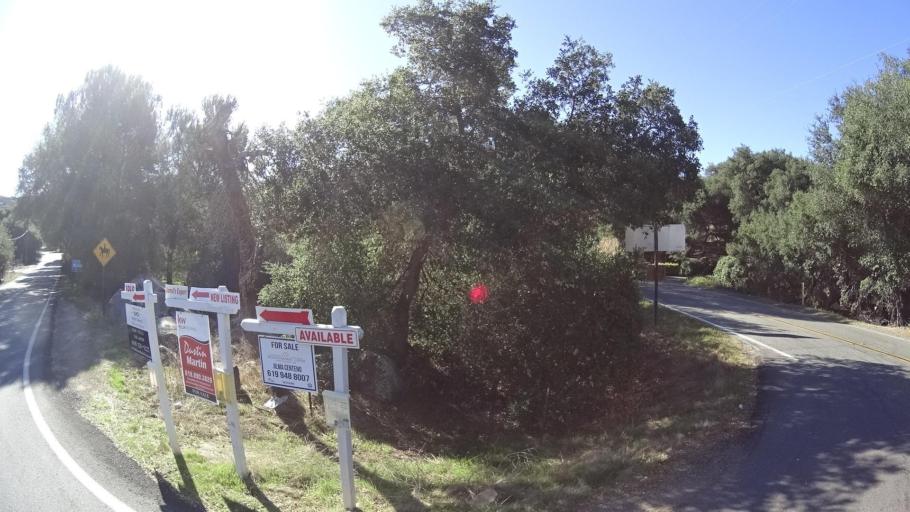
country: US
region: California
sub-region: San Diego County
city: Jamul
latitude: 32.6790
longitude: -116.7530
